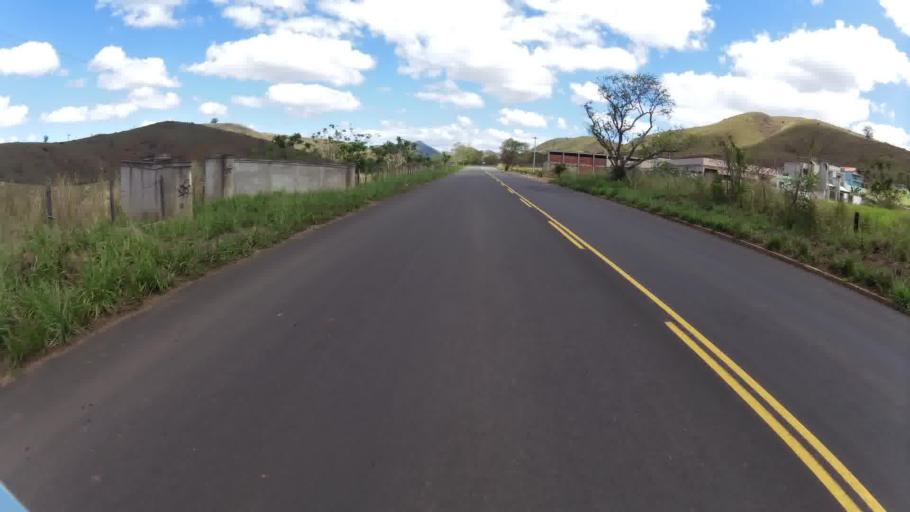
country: BR
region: Rio de Janeiro
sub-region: Itaperuna
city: Itaperuna
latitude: -21.2797
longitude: -41.7895
